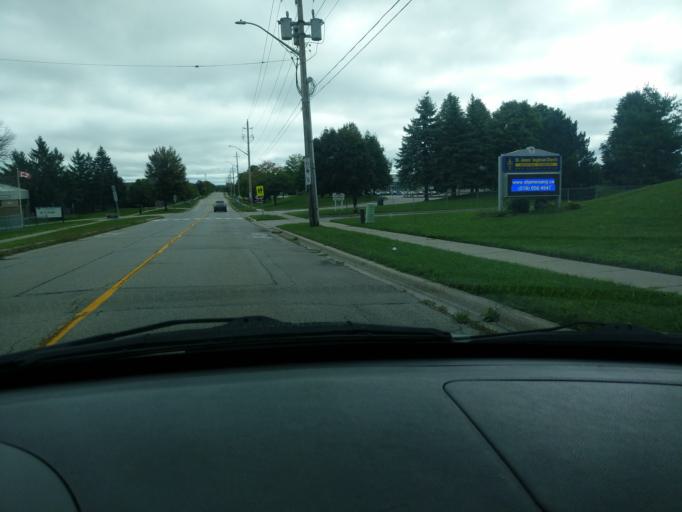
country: CA
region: Ontario
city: Cambridge
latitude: 43.4279
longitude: -80.2953
